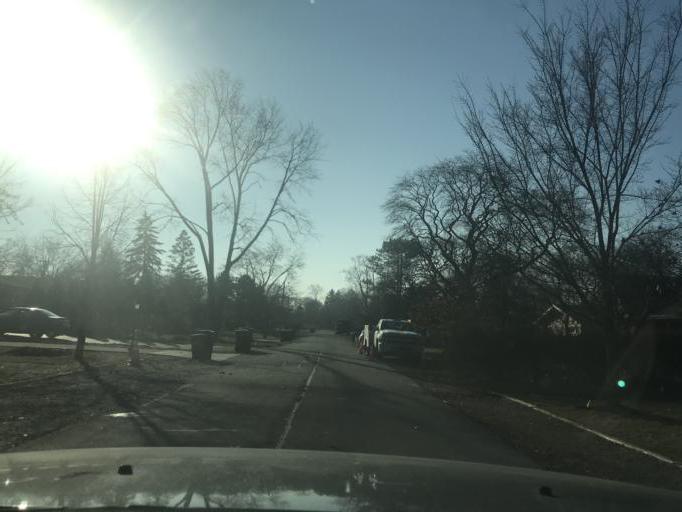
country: US
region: Illinois
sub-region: Cook County
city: Northfield
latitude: 42.0985
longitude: -87.7624
